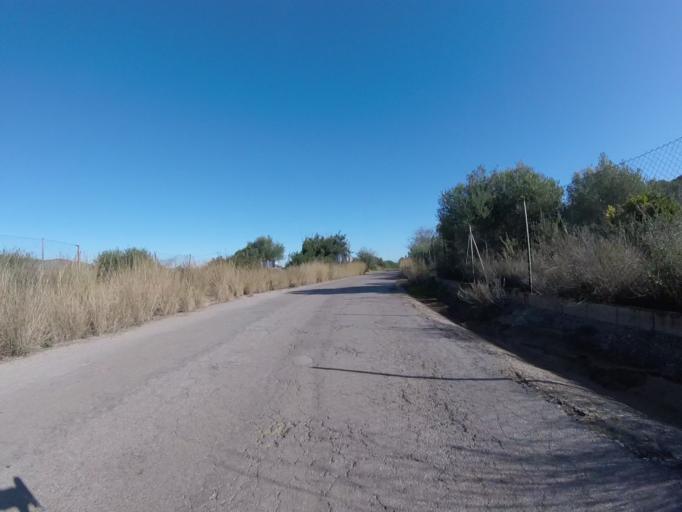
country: ES
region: Valencia
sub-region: Provincia de Castello
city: Orpesa/Oropesa del Mar
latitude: 40.1257
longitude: 0.1172
